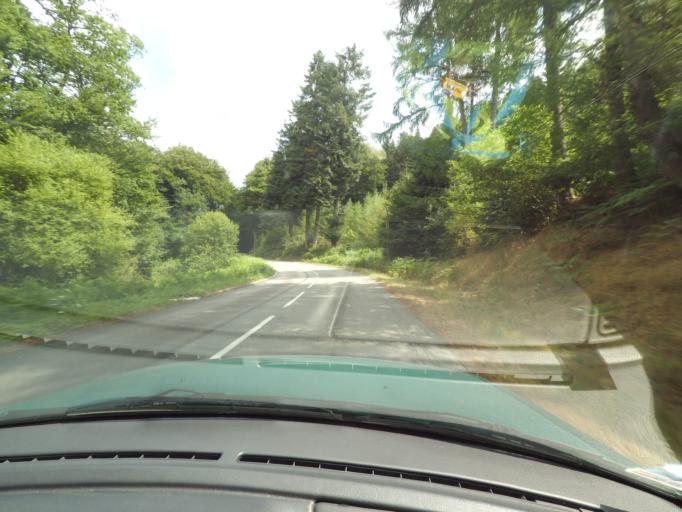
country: FR
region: Limousin
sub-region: Departement de la Haute-Vienne
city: Eymoutiers
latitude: 45.7180
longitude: 1.8594
